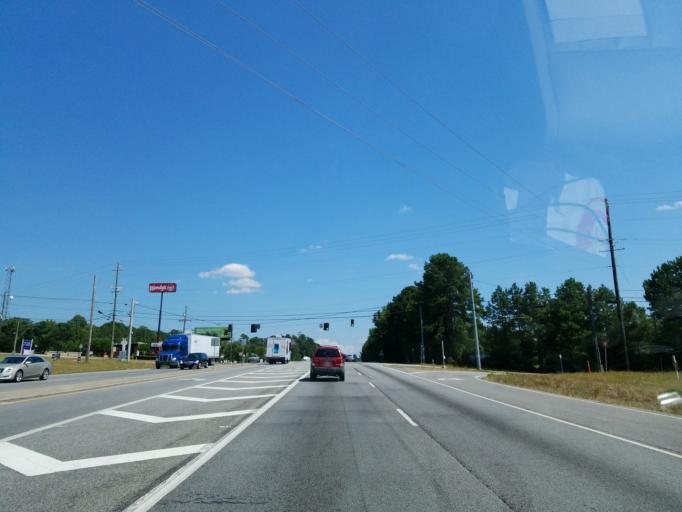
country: US
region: Georgia
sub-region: Henry County
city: Hampton
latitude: 33.3818
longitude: -84.3020
